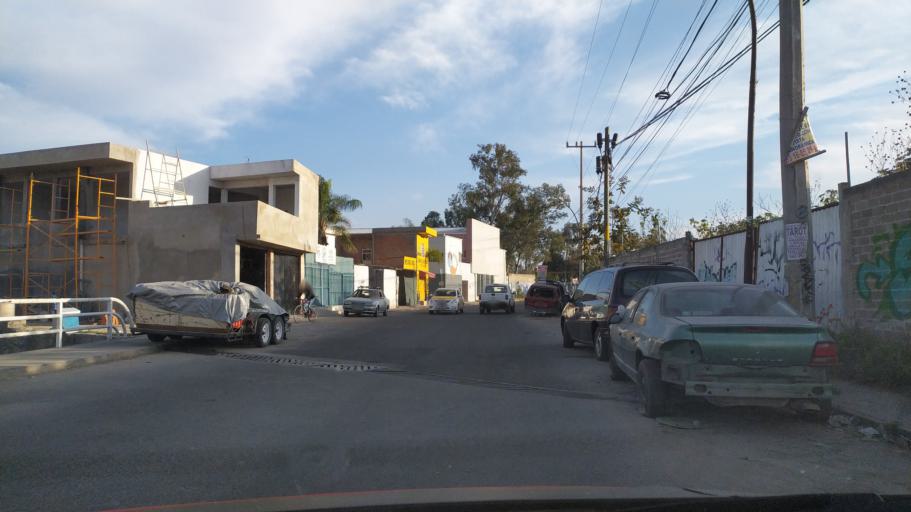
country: MX
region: Jalisco
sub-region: Tlajomulco de Zuniga
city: Palomar
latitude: 20.6278
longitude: -103.4554
